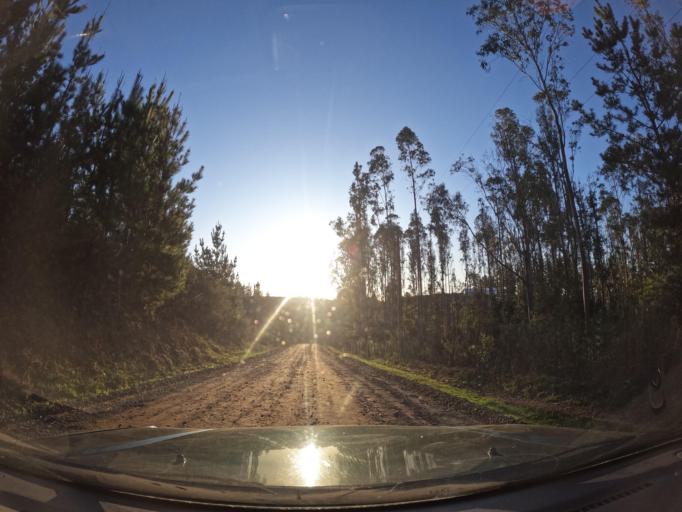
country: CL
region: Biobio
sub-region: Provincia de Concepcion
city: Chiguayante
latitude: -37.0146
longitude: -72.8603
